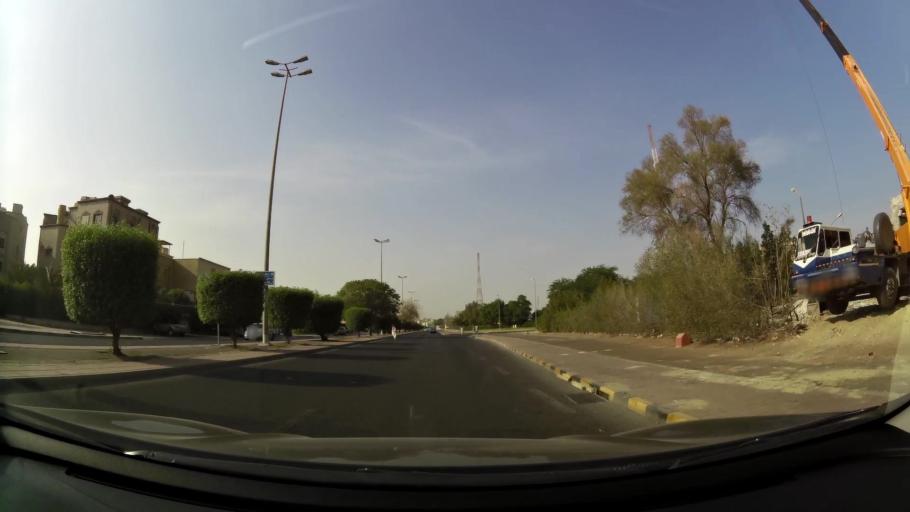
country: KW
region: Mubarak al Kabir
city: Mubarak al Kabir
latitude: 29.1680
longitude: 48.0798
